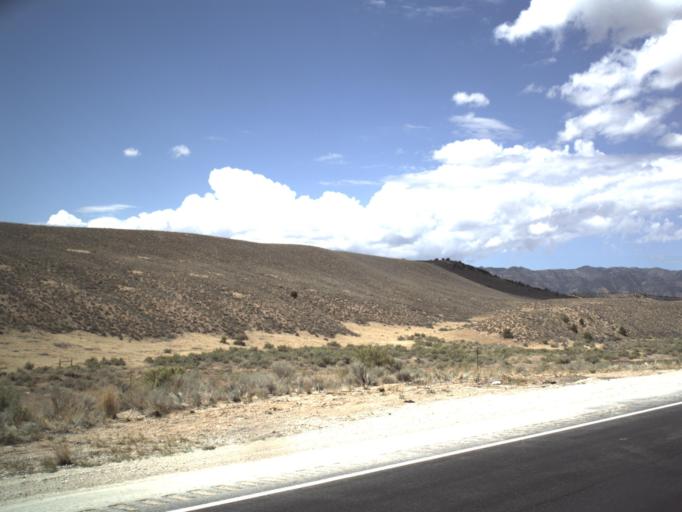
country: US
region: Utah
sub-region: Sevier County
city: Aurora
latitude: 38.9637
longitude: -111.9363
